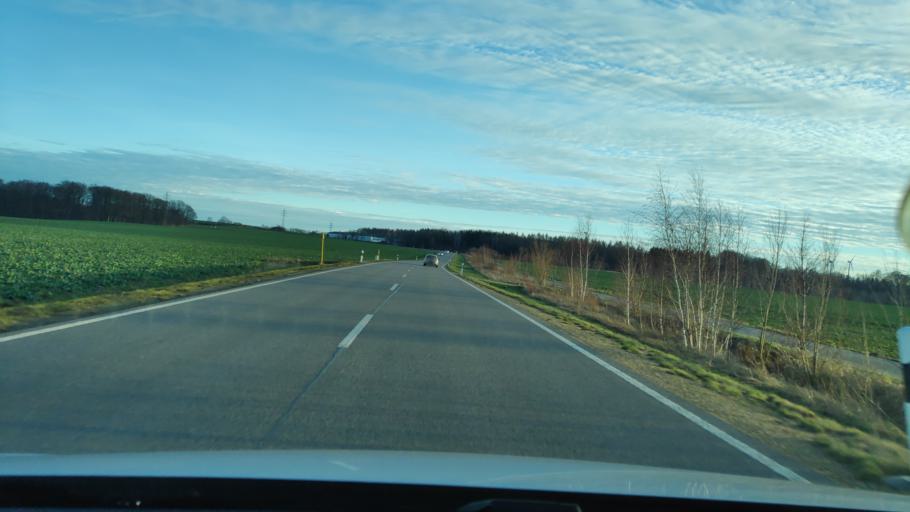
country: DE
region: Saxony
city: Mulsen
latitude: 50.7586
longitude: 12.5353
